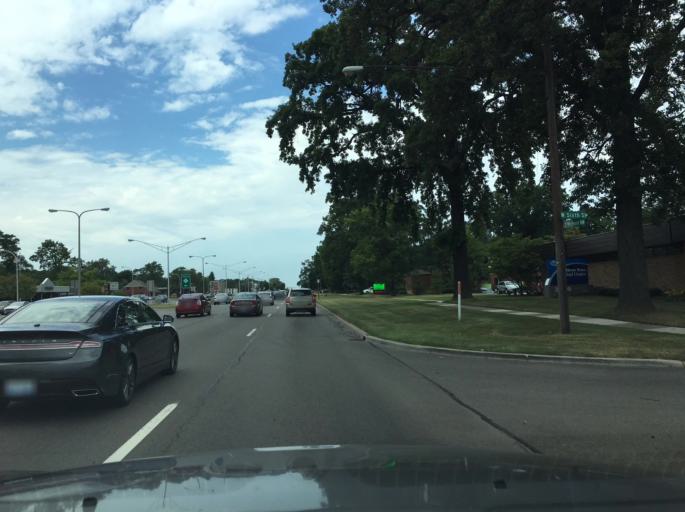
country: US
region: Michigan
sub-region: Oakland County
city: Royal Oak
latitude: 42.4846
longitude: -83.1540
